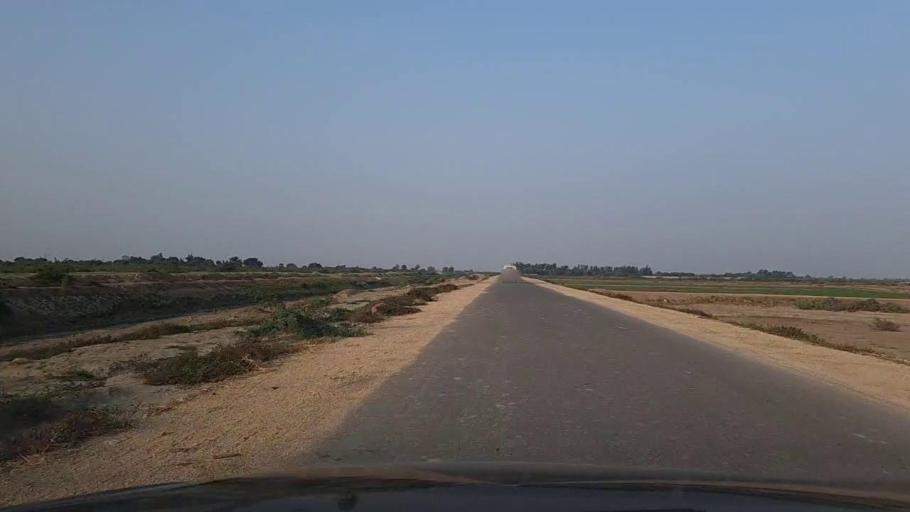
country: PK
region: Sindh
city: Mirpur Sakro
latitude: 24.4495
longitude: 67.7904
